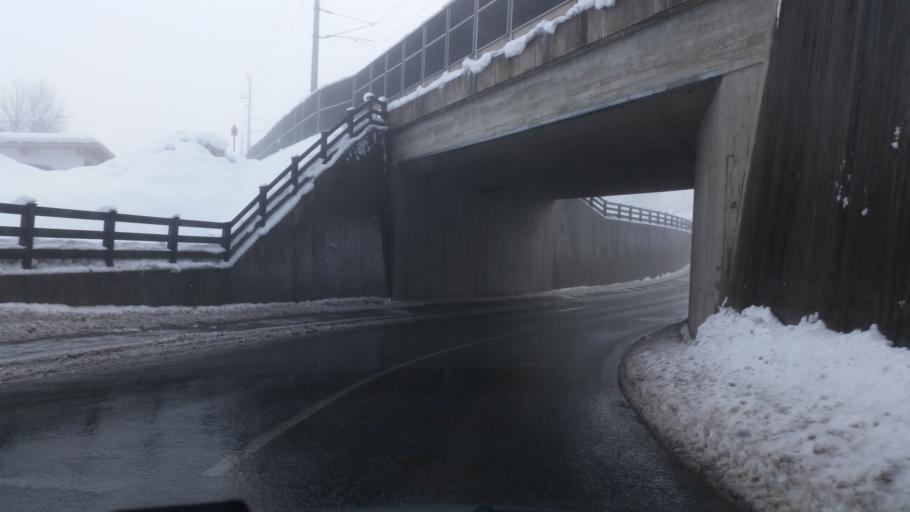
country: AT
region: Tyrol
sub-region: Politischer Bezirk Kitzbuhel
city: Sankt Johann in Tirol
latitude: 47.5198
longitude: 12.4377
